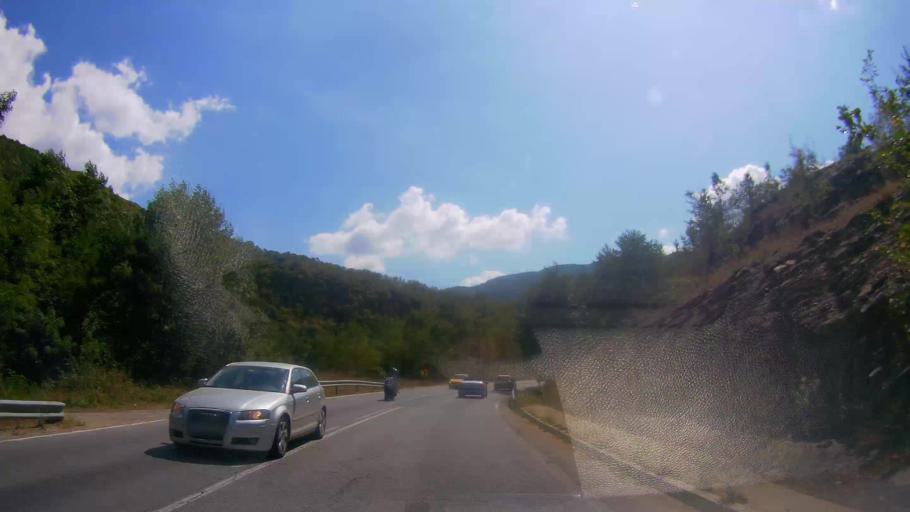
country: BG
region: Stara Zagora
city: Gurkovo
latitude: 42.7148
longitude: 25.7182
